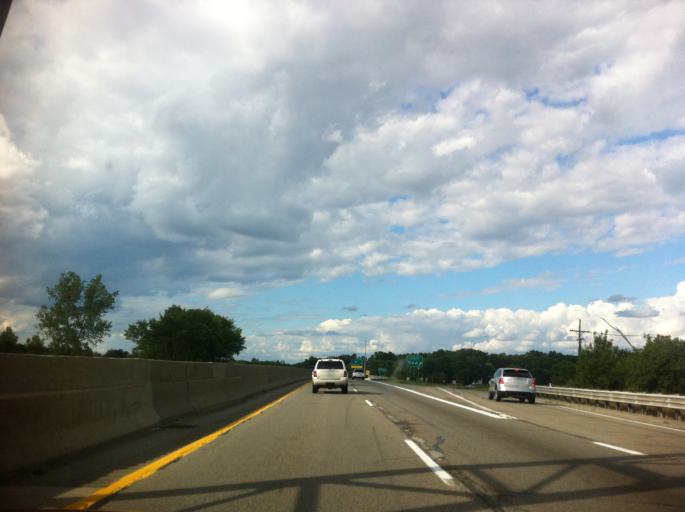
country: US
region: Michigan
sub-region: Livingston County
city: Whitmore Lake
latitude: 42.4390
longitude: -83.7563
